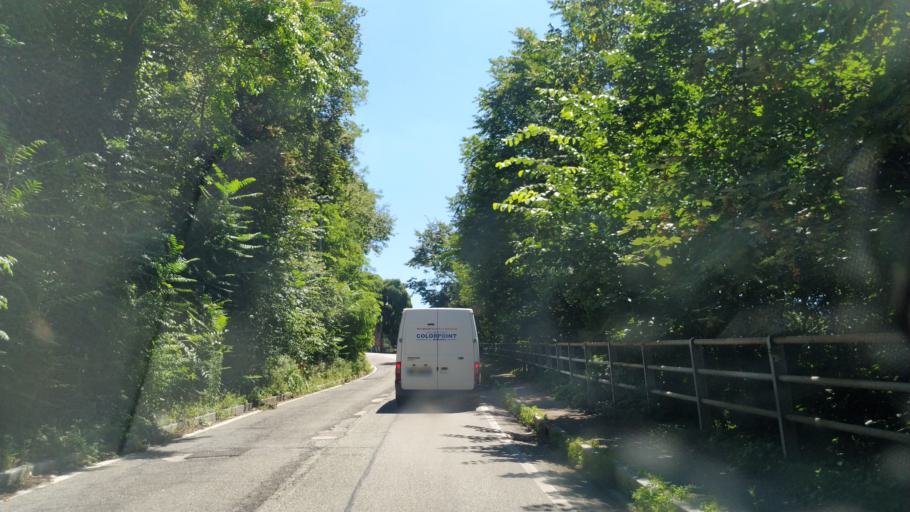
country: IT
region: Piedmont
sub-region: Provincia di Torino
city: San Mauro Torinese
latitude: 45.0816
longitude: 7.7452
